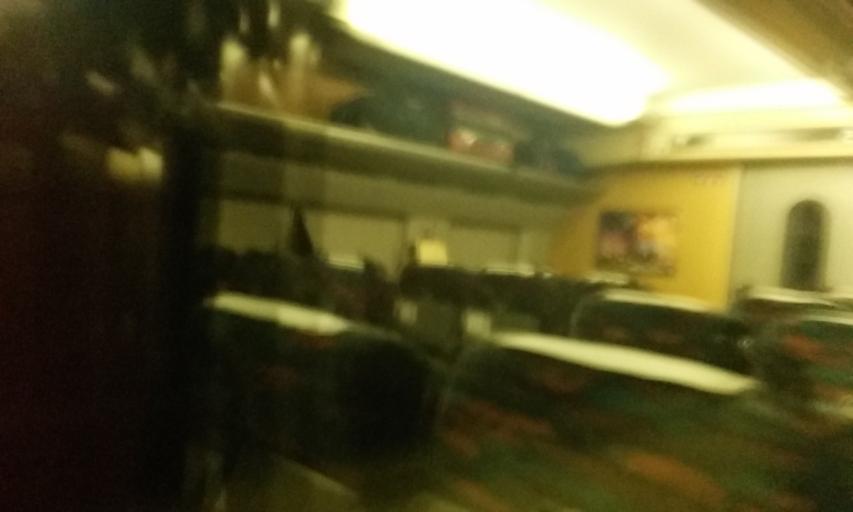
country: JP
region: Miyagi
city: Iwanuma
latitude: 38.1597
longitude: 140.8464
